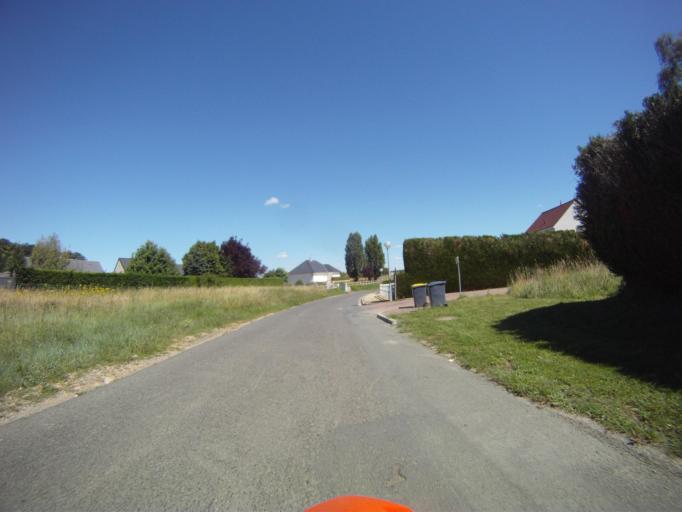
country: FR
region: Centre
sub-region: Departement d'Indre-et-Loire
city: Rochecorbon
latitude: 47.4241
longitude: 0.7769
